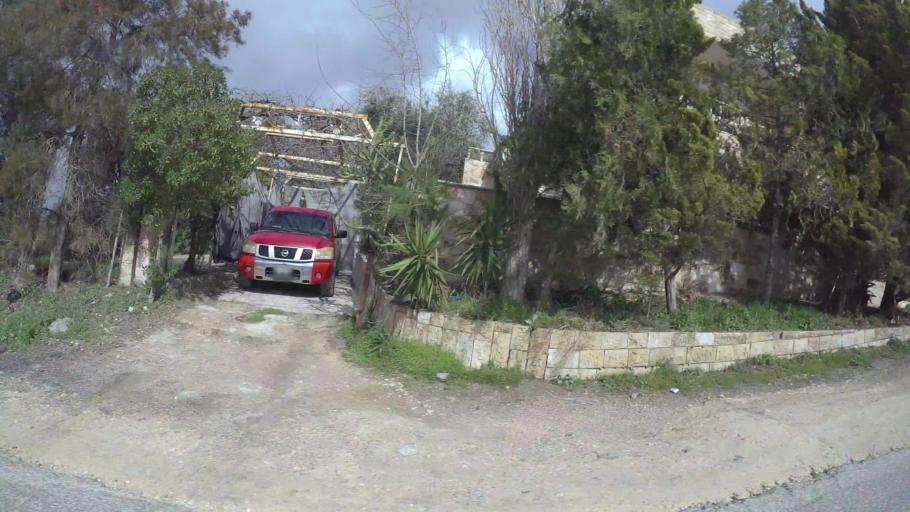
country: JO
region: Amman
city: Al Jubayhah
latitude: 32.0728
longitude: 35.8635
